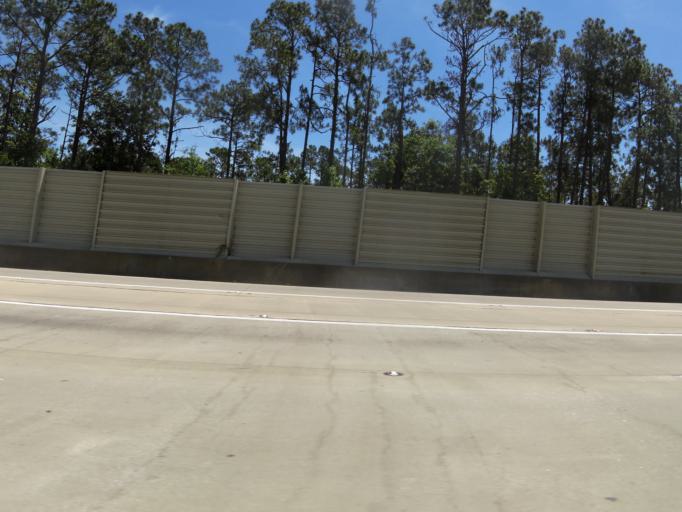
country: US
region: Georgia
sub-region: Glynn County
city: Dock Junction
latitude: 31.2453
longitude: -81.5003
